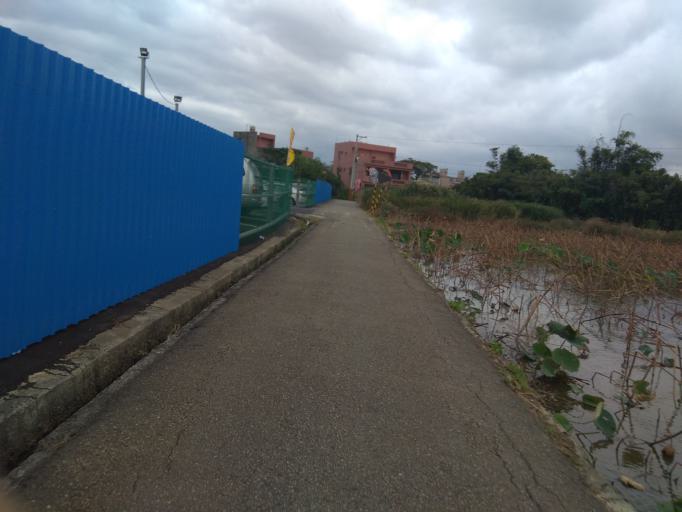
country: TW
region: Taiwan
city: Taoyuan City
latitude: 25.0536
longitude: 121.2197
